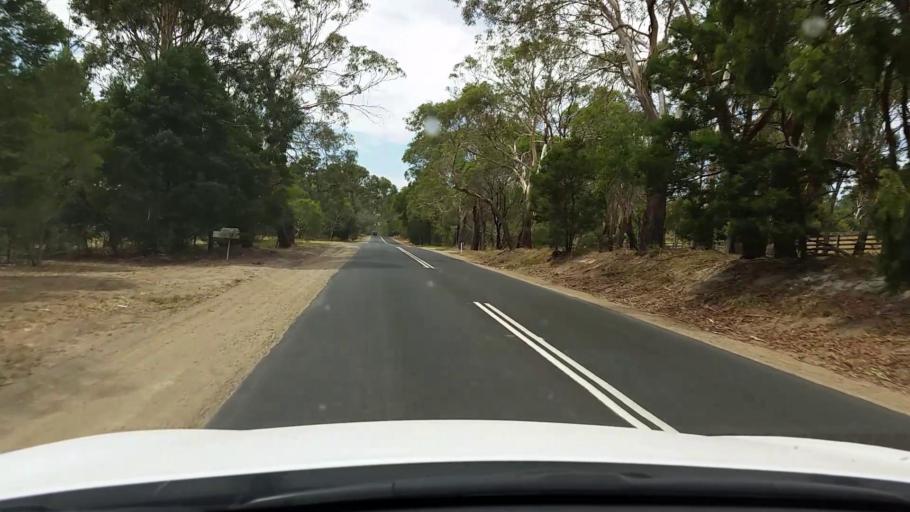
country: AU
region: Victoria
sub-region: Mornington Peninsula
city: Mount Martha
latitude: -38.2866
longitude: 145.0622
